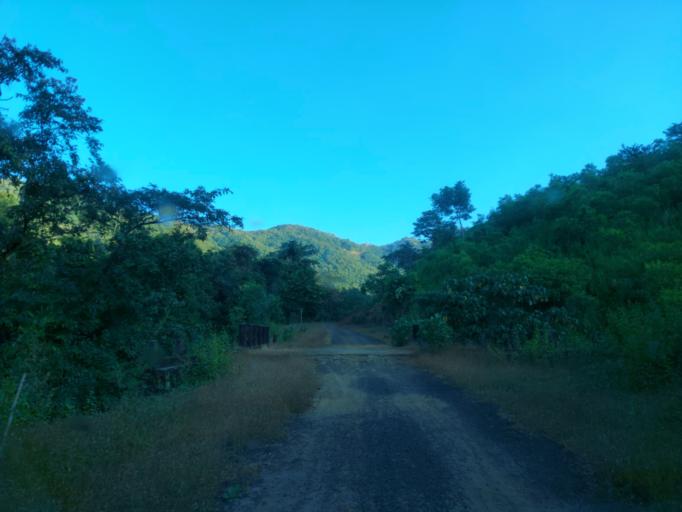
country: IN
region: Maharashtra
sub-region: Sindhudurg
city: Kudal
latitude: 16.0774
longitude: 73.8266
